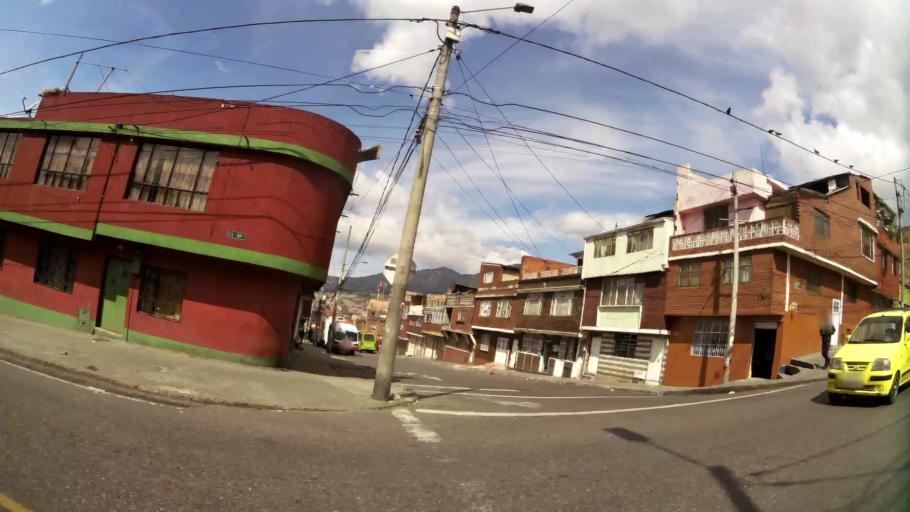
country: CO
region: Bogota D.C.
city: Bogota
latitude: 4.5644
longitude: -74.1004
